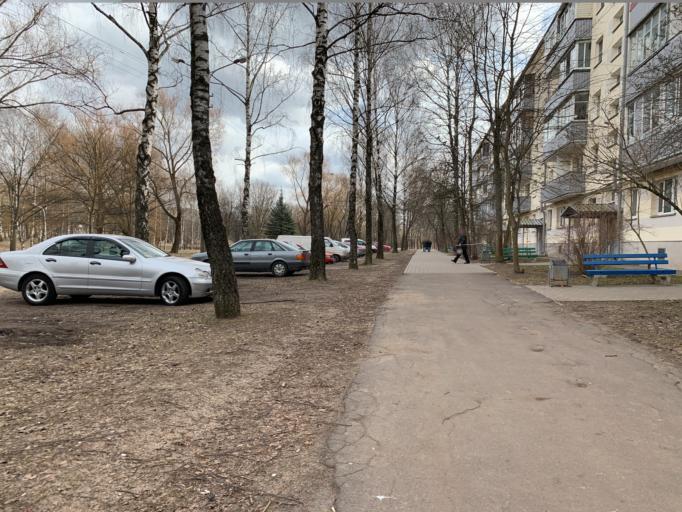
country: BY
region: Minsk
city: Borovlyany
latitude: 53.9520
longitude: 27.6267
